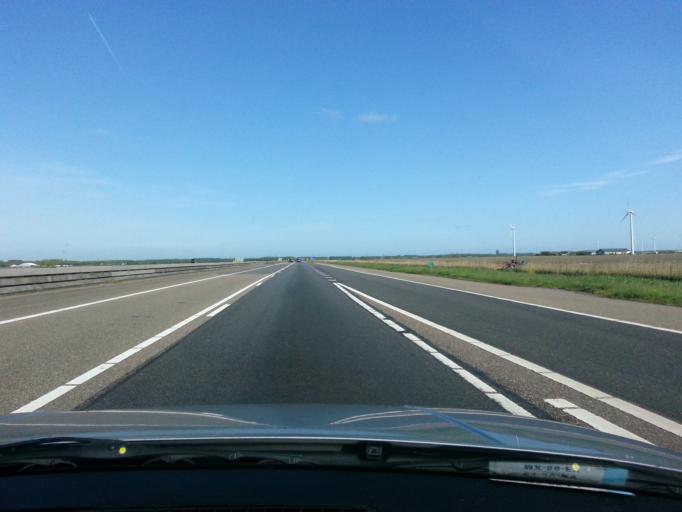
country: NL
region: North Holland
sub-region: Gemeente Huizen
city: Huizen
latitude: 52.3522
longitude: 5.3339
